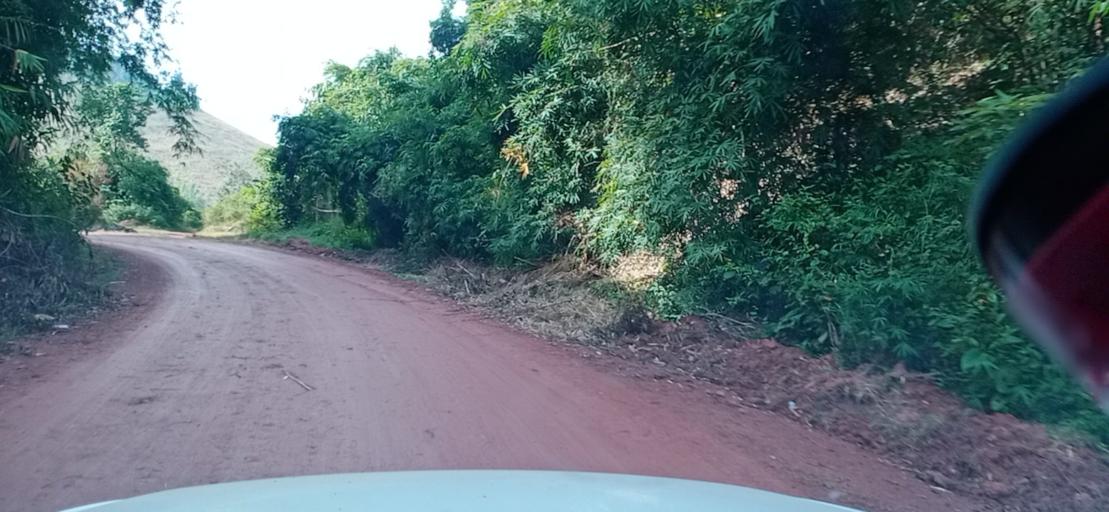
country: TH
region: Changwat Bueng Kan
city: Pak Khat
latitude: 18.6709
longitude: 103.1947
